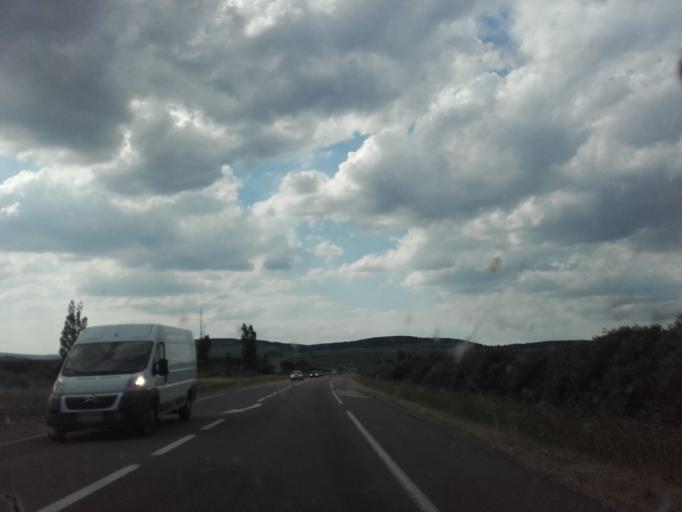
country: FR
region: Bourgogne
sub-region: Departement de la Cote-d'Or
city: Bligny-les-Beaune
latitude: 47.0072
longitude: 4.8232
